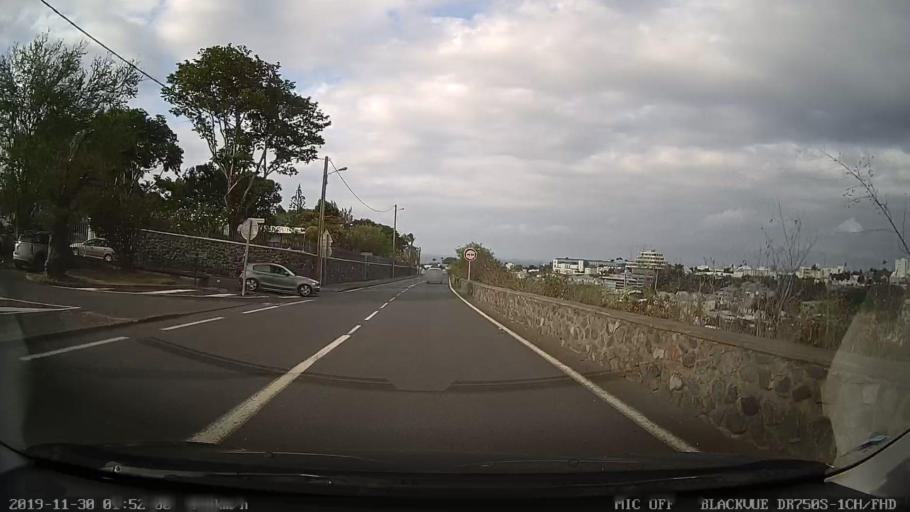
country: RE
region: Reunion
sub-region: Reunion
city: Saint-Denis
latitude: -20.8835
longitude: 55.4440
